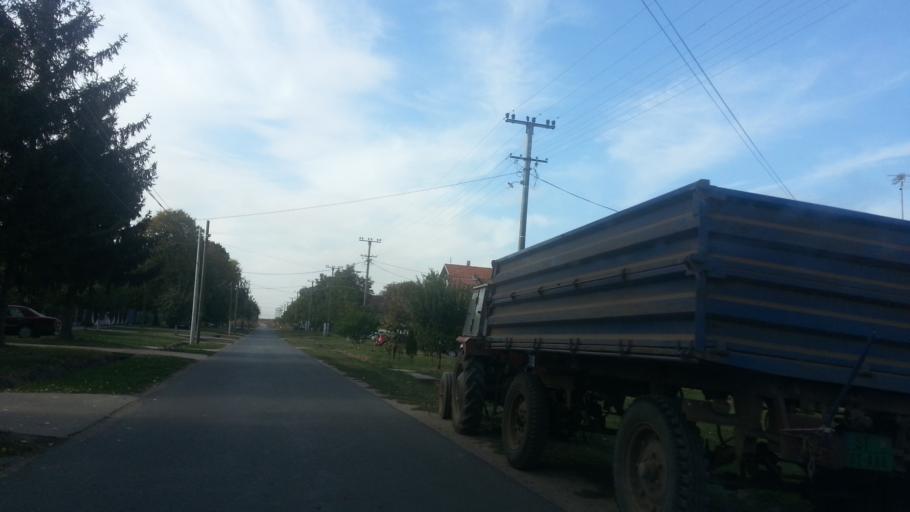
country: RS
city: Belegis
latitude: 45.0203
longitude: 20.3168
